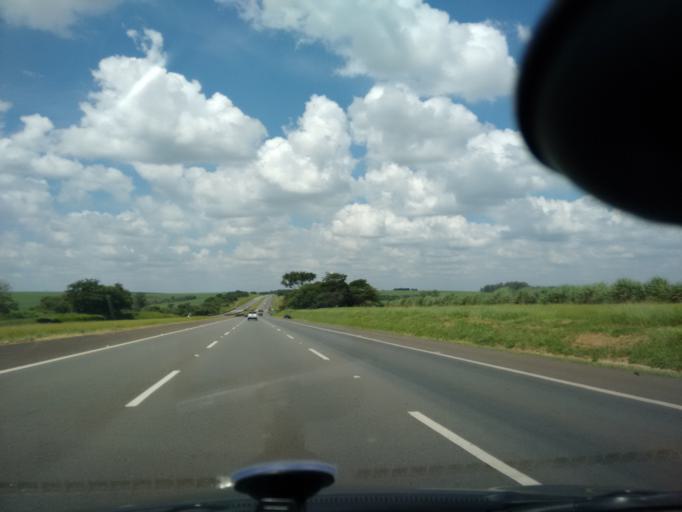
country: BR
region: Sao Paulo
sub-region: Santa Barbara D'Oeste
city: Santa Barbara d'Oeste
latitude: -22.7956
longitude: -47.4112
